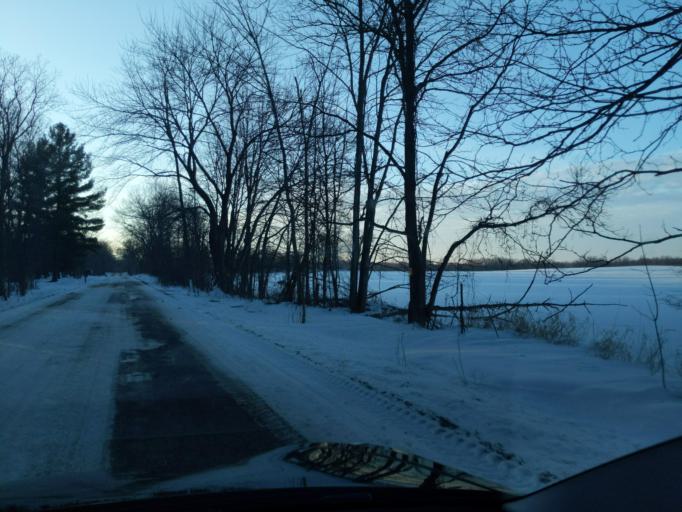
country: US
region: Michigan
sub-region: Ingham County
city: Webberville
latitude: 42.5686
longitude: -84.1551
